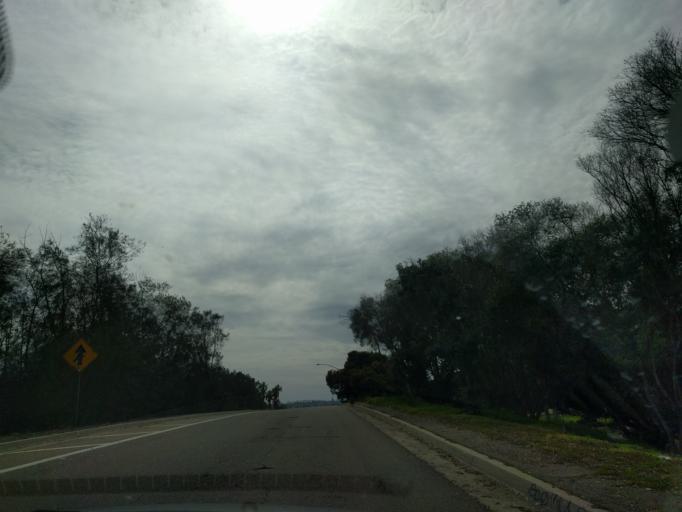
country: US
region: California
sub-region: San Diego County
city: San Diego
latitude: 32.7611
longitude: -117.2323
